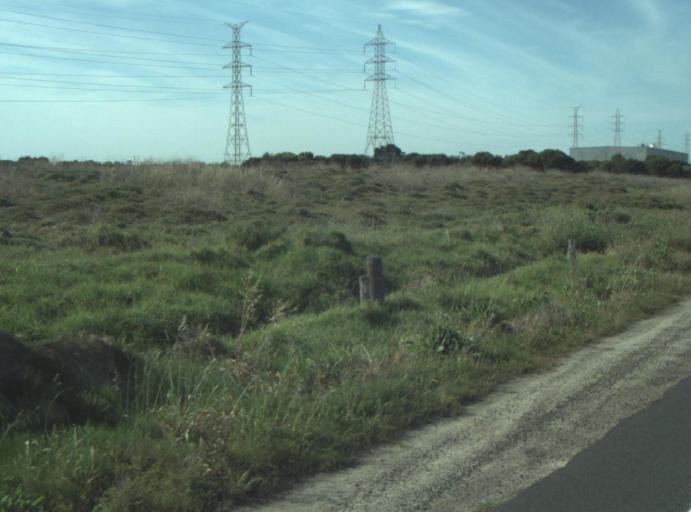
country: AU
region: Victoria
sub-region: Greater Geelong
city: Leopold
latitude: -38.1537
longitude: 144.4327
